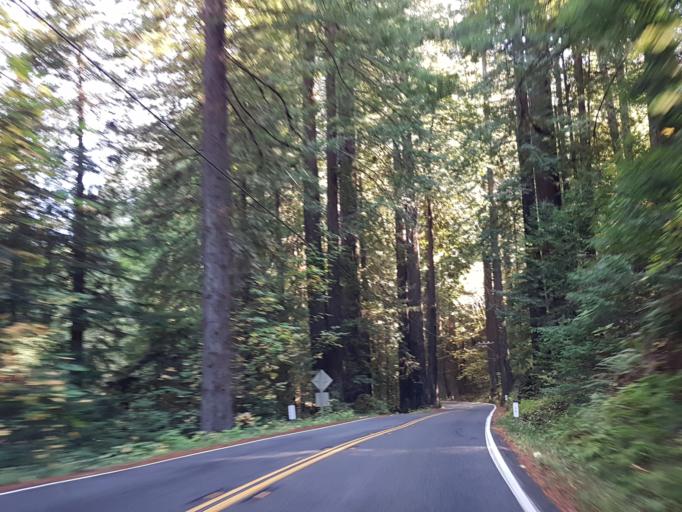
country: US
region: California
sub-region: Humboldt County
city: Rio Dell
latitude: 40.4184
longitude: -123.9767
